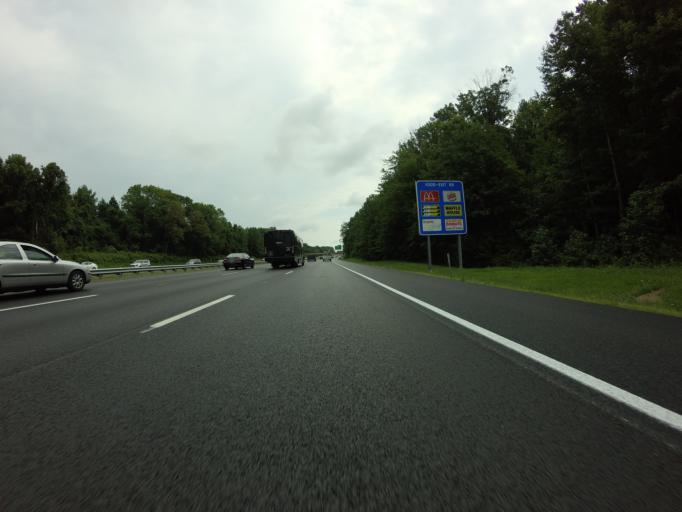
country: US
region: Maryland
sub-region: Harford County
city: Aberdeen
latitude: 39.5535
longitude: -76.1582
